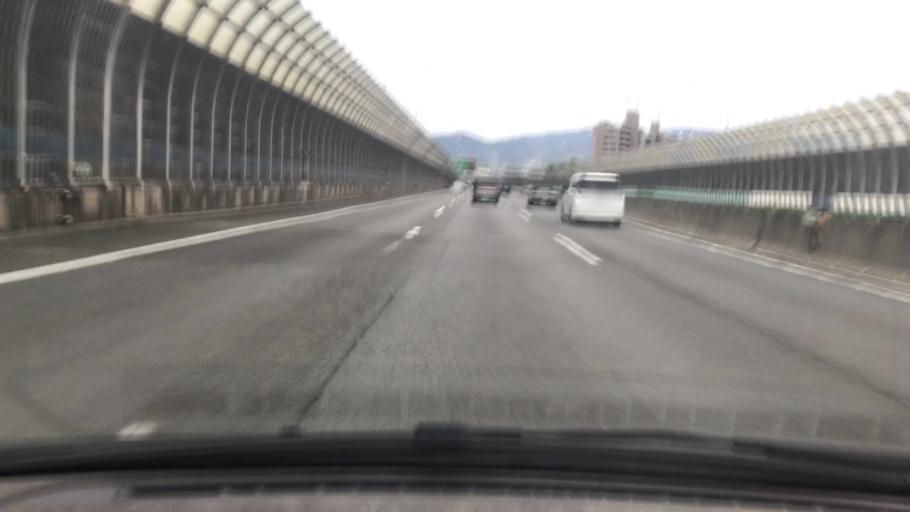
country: JP
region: Kyoto
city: Muko
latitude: 34.9482
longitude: 135.7306
